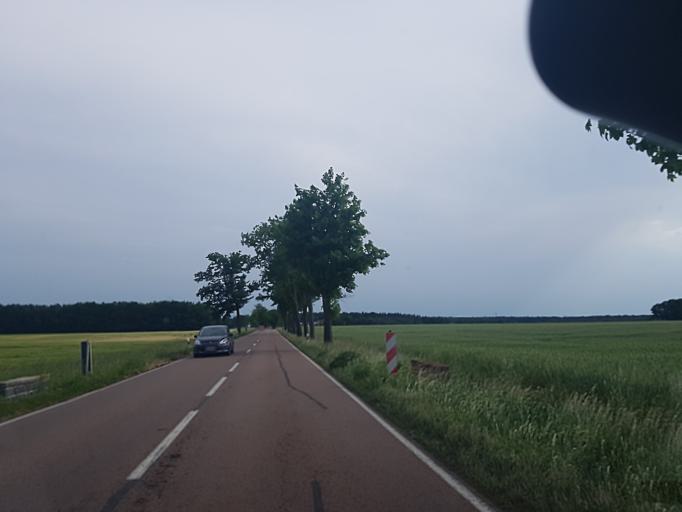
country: DE
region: Saxony-Anhalt
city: Nudersdorf
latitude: 51.9173
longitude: 12.6060
